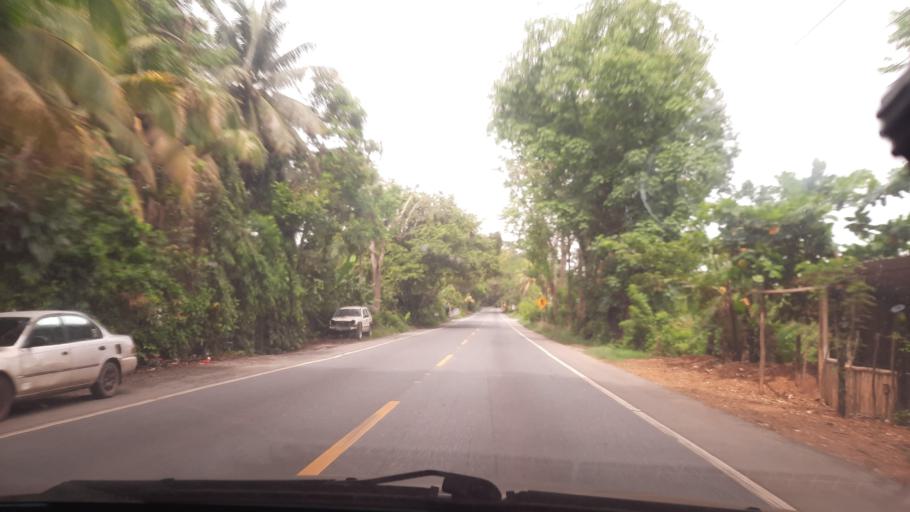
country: GT
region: Izabal
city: Morales
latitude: 15.5126
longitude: -88.8027
